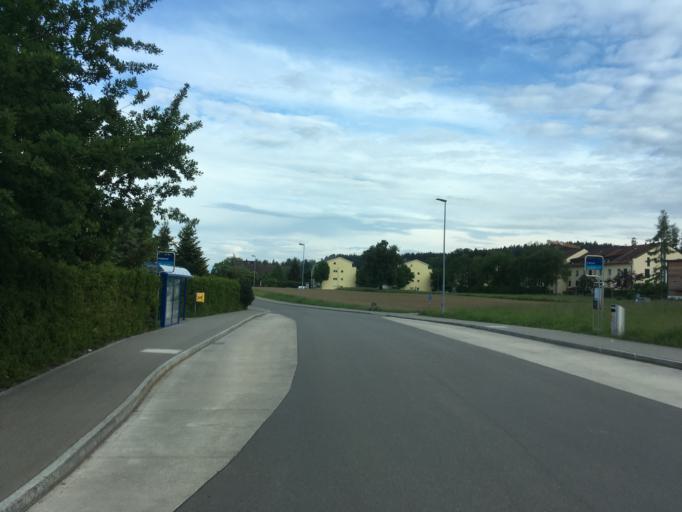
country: CH
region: Zurich
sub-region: Bezirk Uster
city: Binz
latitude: 47.3594
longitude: 8.6245
